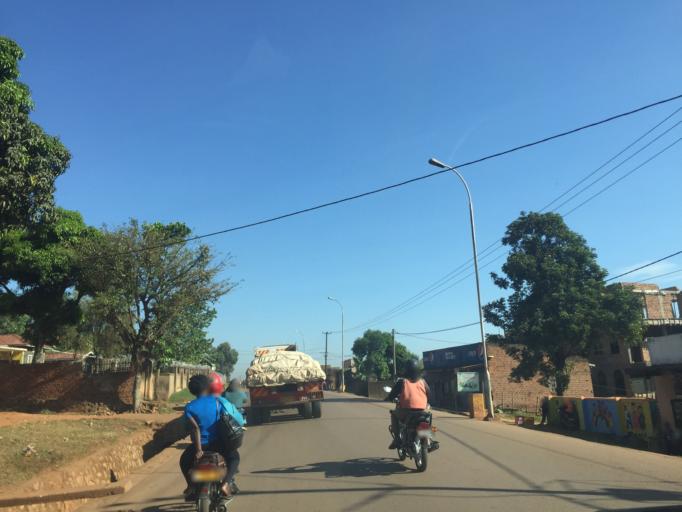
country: UG
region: Central Region
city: Kampala Central Division
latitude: 0.3690
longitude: 32.5692
